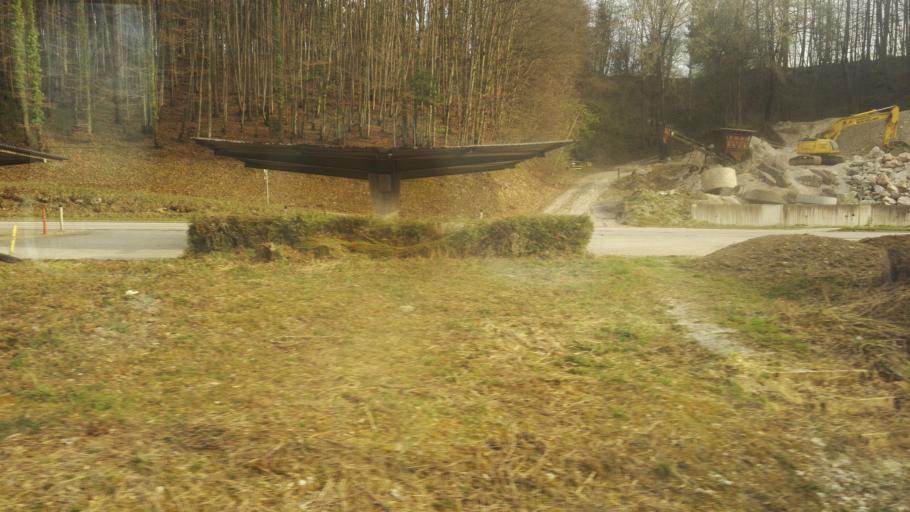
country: AT
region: Upper Austria
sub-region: Politischer Bezirk Gmunden
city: Altmunster
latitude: 47.9195
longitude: 13.7739
